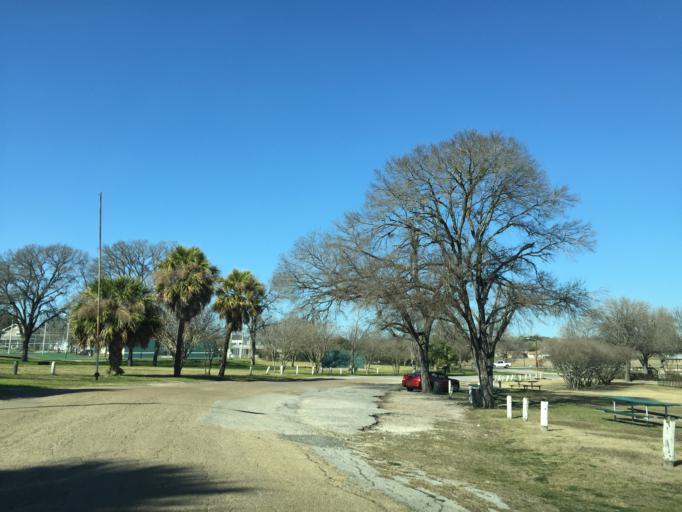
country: US
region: Texas
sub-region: Williamson County
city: Taylor
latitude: 30.5804
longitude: -97.4156
